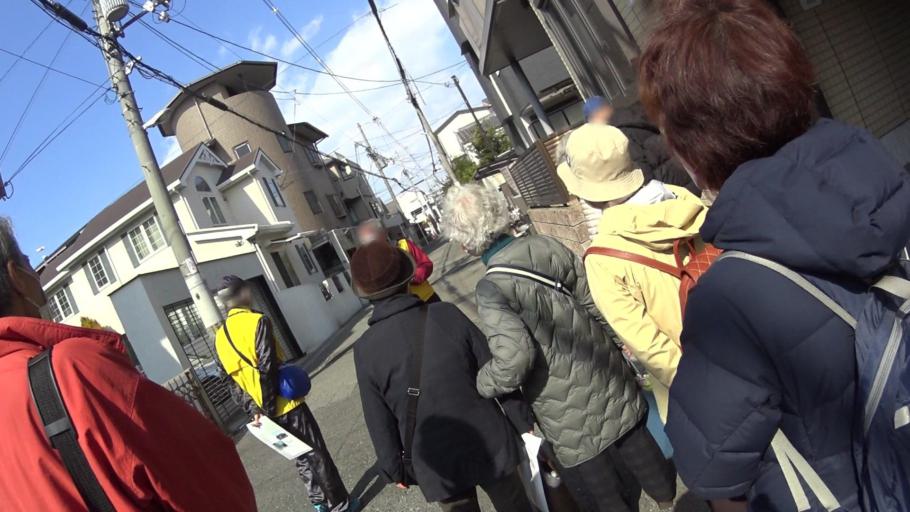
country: JP
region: Osaka
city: Sakai
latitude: 34.6199
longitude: 135.4939
